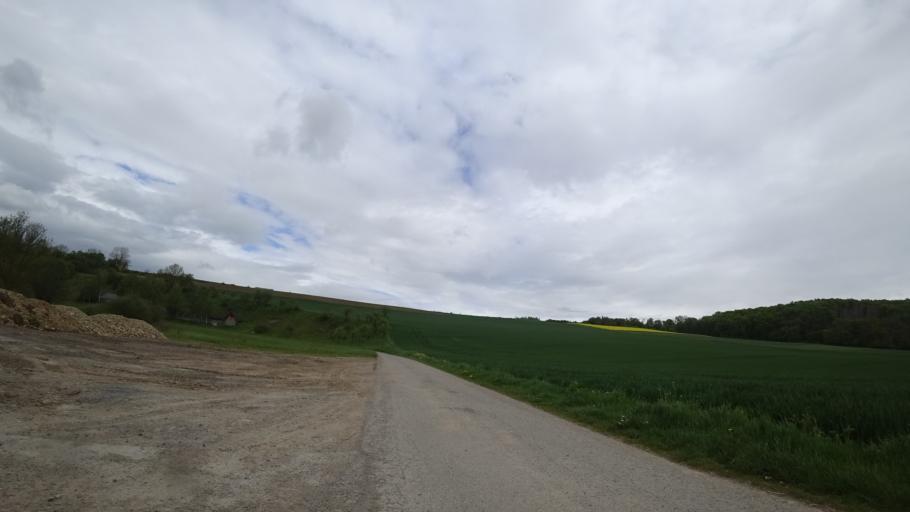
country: DE
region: Hesse
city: Liebenau
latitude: 51.4588
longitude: 9.3191
